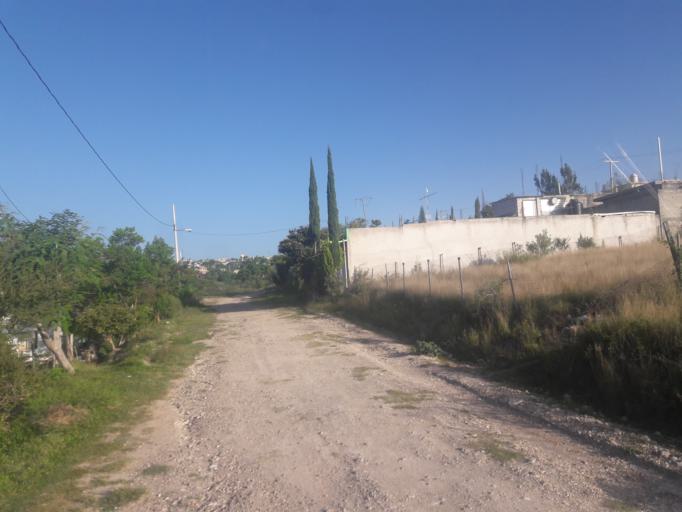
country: MX
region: Oaxaca
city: Ciudad de Huajuapam de Leon
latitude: 17.8036
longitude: -97.7948
